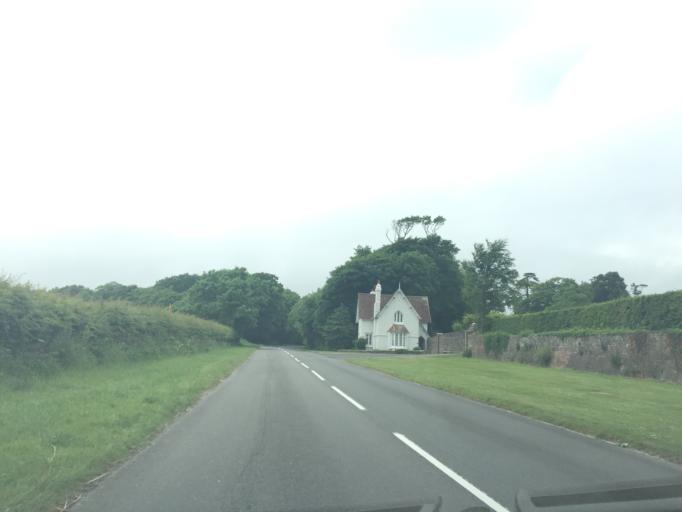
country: GB
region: England
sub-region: Dorset
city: Wool
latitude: 50.6363
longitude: -2.2103
